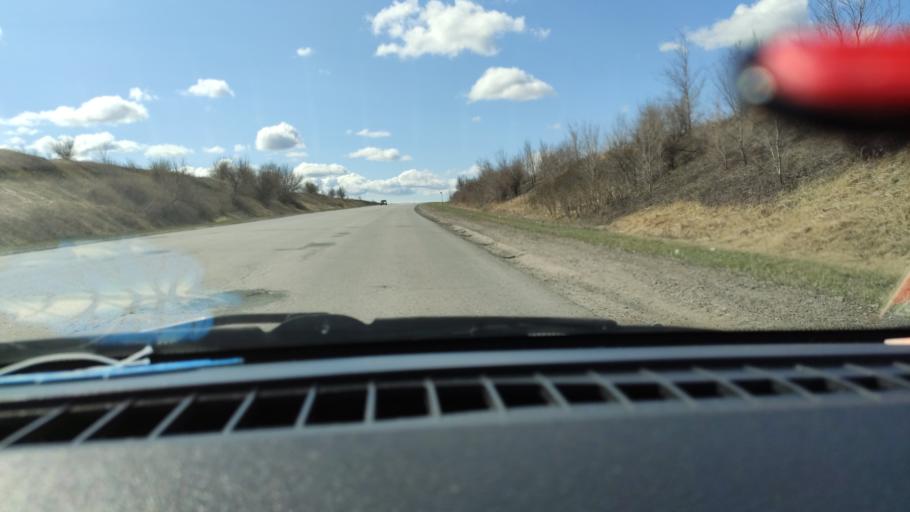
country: RU
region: Samara
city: Varlamovo
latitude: 53.0605
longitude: 48.3511
